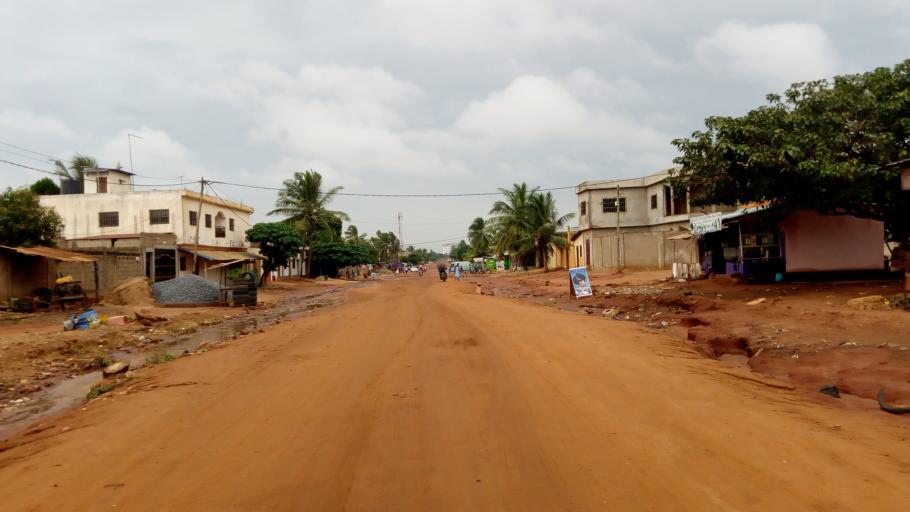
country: TG
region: Maritime
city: Lome
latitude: 6.2302
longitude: 1.1816
